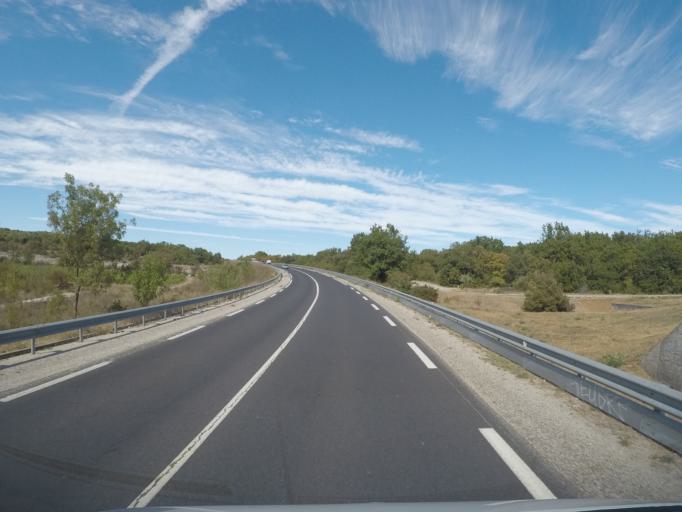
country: FR
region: Languedoc-Roussillon
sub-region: Departement de l'Herault
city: Saint-Martin-de-Londres
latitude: 43.7966
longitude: 3.7399
